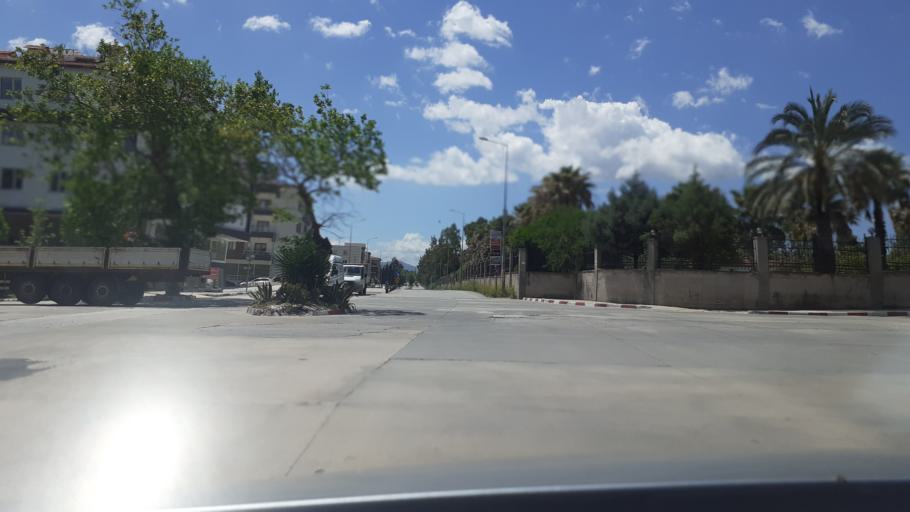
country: TR
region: Hatay
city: Anayazi
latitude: 36.3283
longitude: 36.1990
